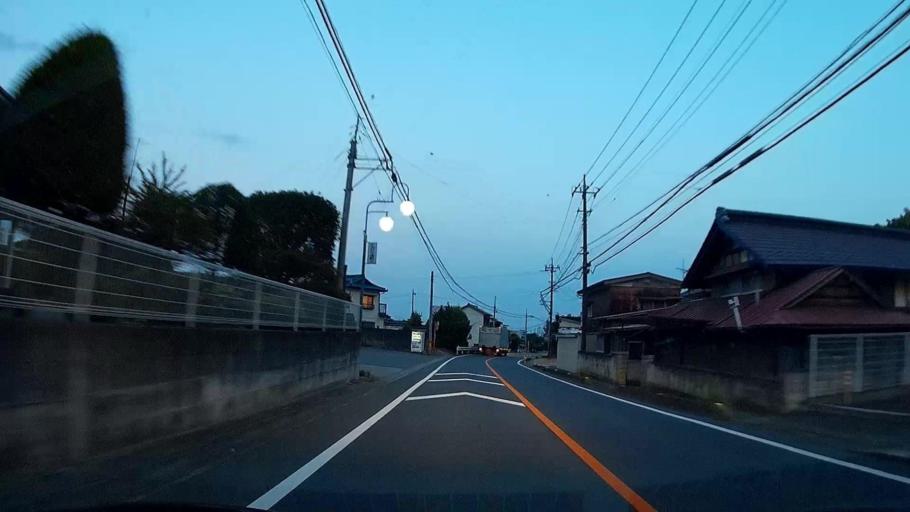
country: JP
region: Gunma
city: Annaka
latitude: 36.3735
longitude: 138.8990
